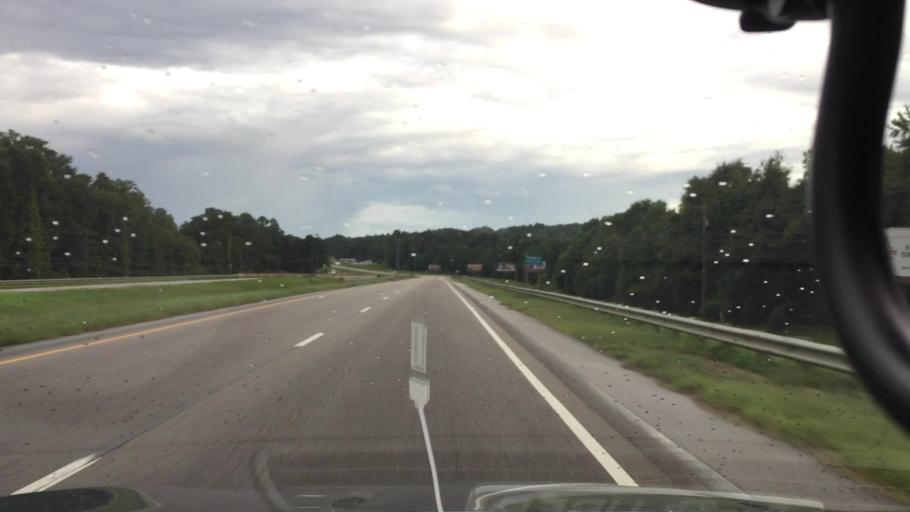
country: US
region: Alabama
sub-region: Pike County
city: Troy
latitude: 31.8466
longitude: -85.9951
